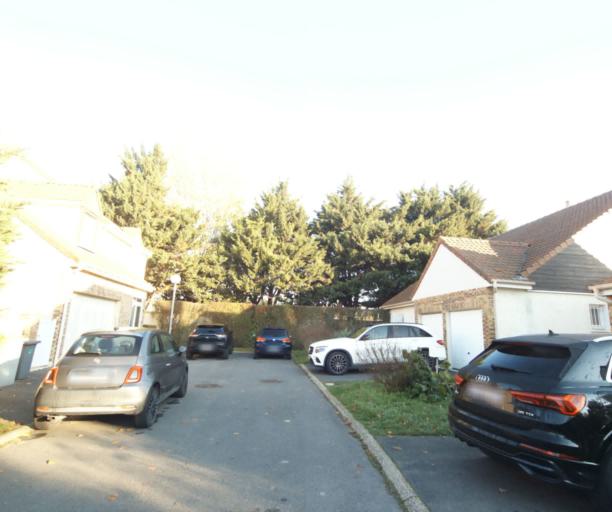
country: FR
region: Ile-de-France
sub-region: Departement du Val-d'Oise
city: Arnouville
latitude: 49.0004
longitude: 2.4306
